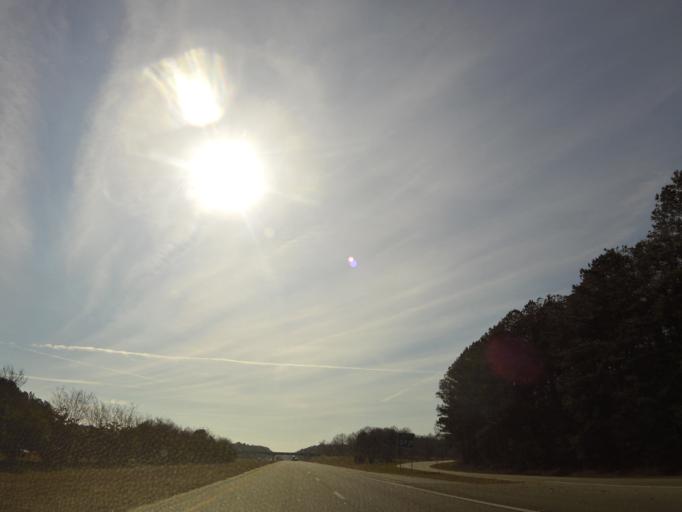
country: US
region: Georgia
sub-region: Harris County
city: Pine Mountain
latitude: 32.8603
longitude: -84.9748
